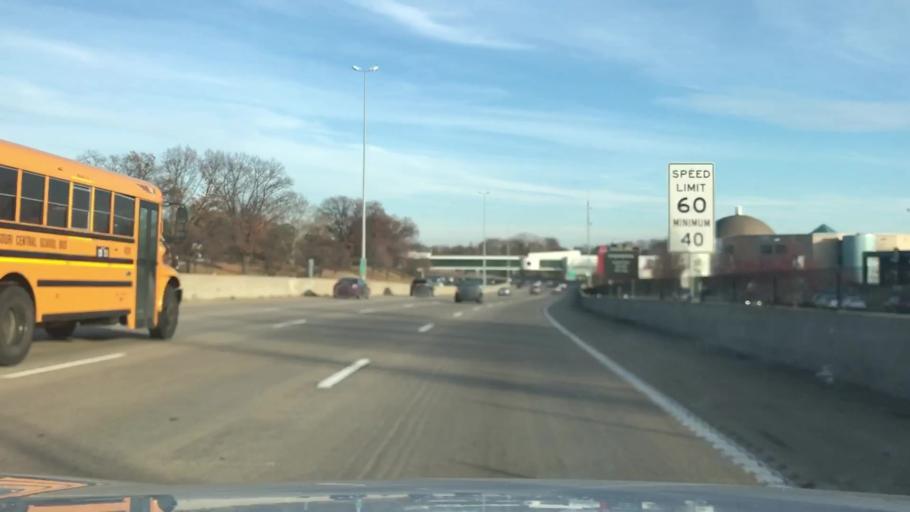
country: US
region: Missouri
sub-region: Saint Louis County
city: University City
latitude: 38.6299
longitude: -90.2745
